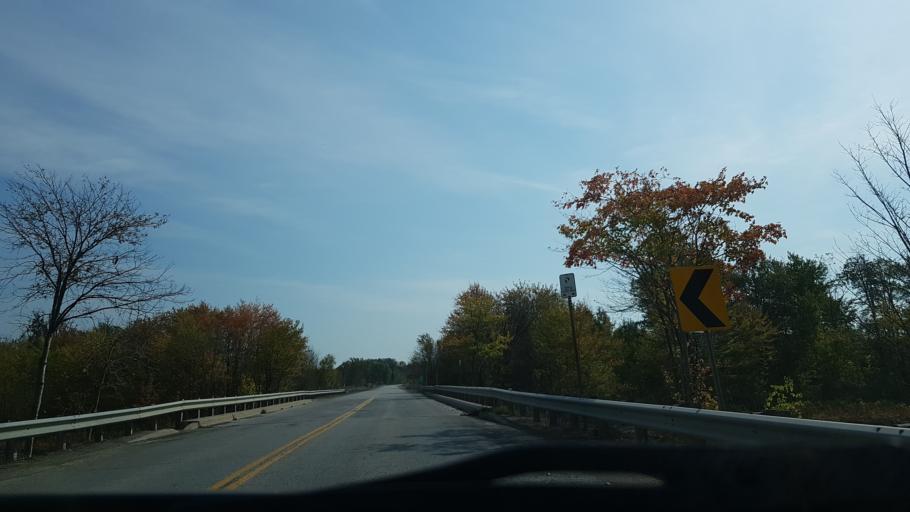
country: CA
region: Ontario
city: Orillia
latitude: 44.6411
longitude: -79.1117
